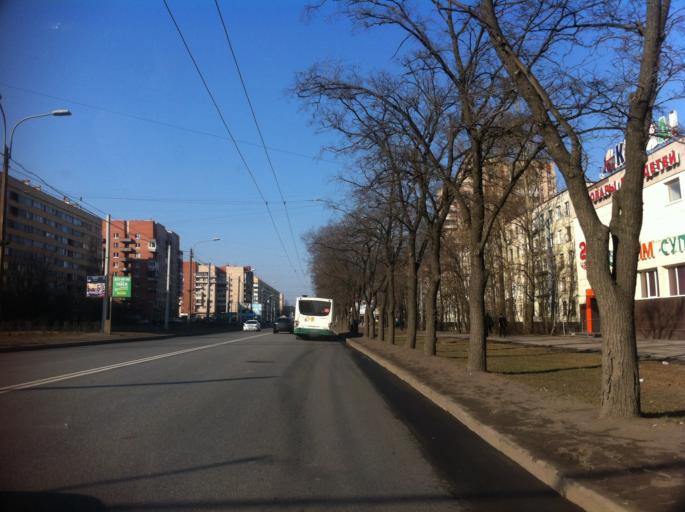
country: RU
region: St.-Petersburg
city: Dachnoye
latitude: 59.8493
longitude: 30.2564
